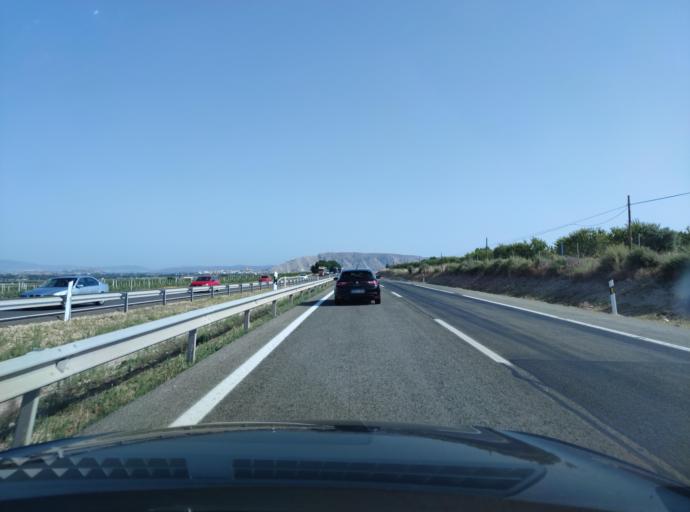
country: ES
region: Valencia
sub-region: Provincia de Alicante
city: Sax
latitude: 38.5847
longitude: -0.8435
